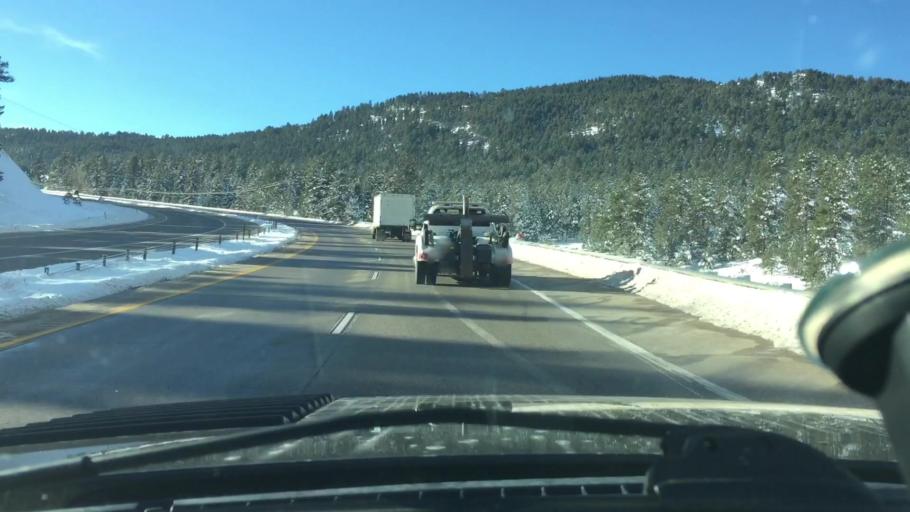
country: US
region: Colorado
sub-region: Jefferson County
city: Indian Hills
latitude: 39.5756
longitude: -105.2392
